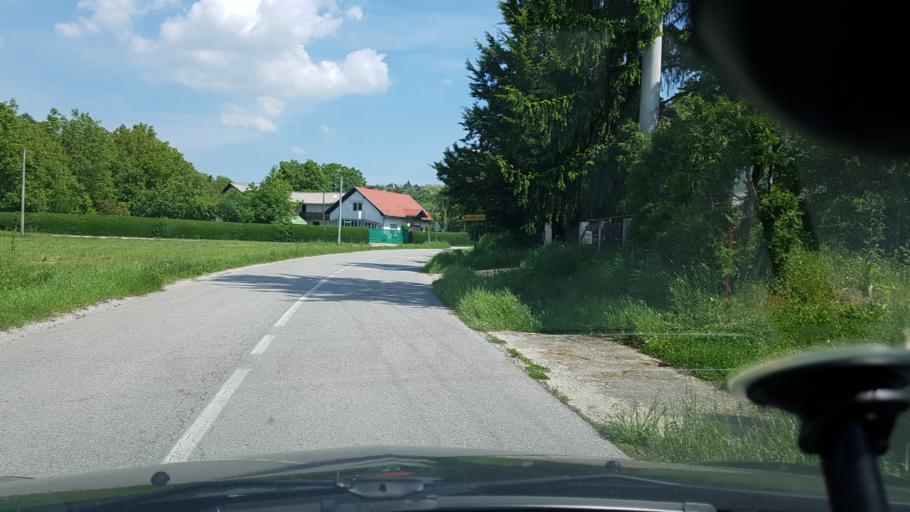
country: HR
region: Krapinsko-Zagorska
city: Marija Bistrica
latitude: 45.9362
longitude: 16.2001
